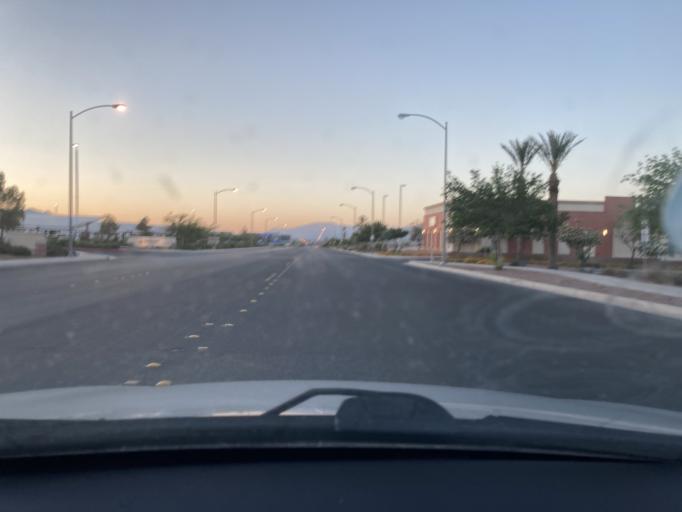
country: US
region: Nevada
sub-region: Clark County
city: Enterprise
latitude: 36.0569
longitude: -115.2701
